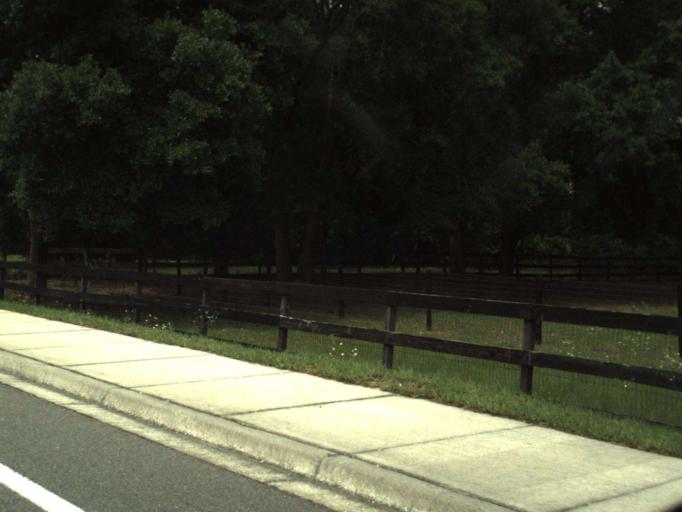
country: US
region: Florida
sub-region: Marion County
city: Silver Springs Shores
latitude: 29.1845
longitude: -82.0535
